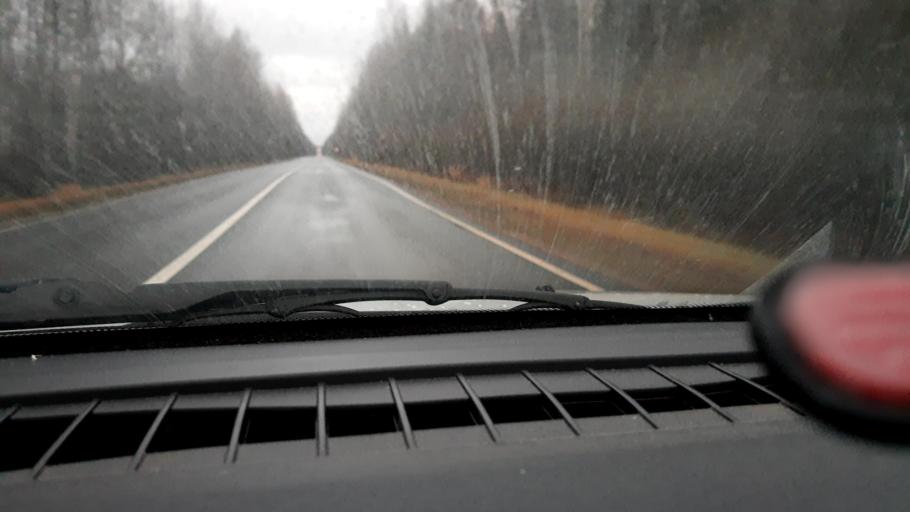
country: RU
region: Nizjnij Novgorod
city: Uren'
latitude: 57.2510
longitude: 45.6042
